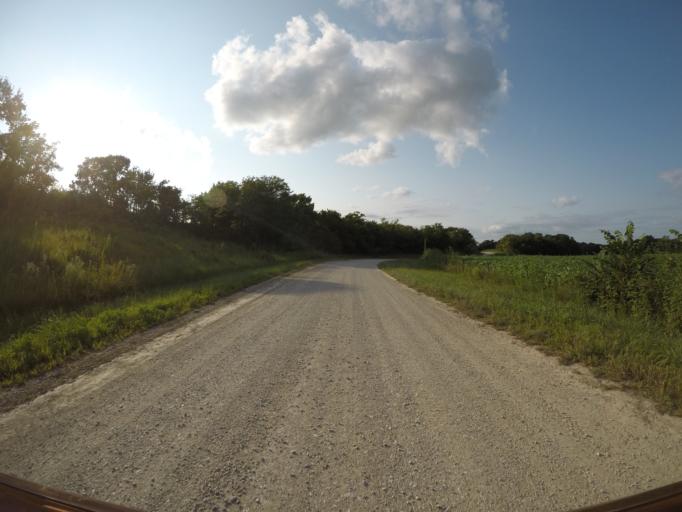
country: US
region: Kansas
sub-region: Wabaunsee County
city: Alma
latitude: 38.8859
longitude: -96.2086
